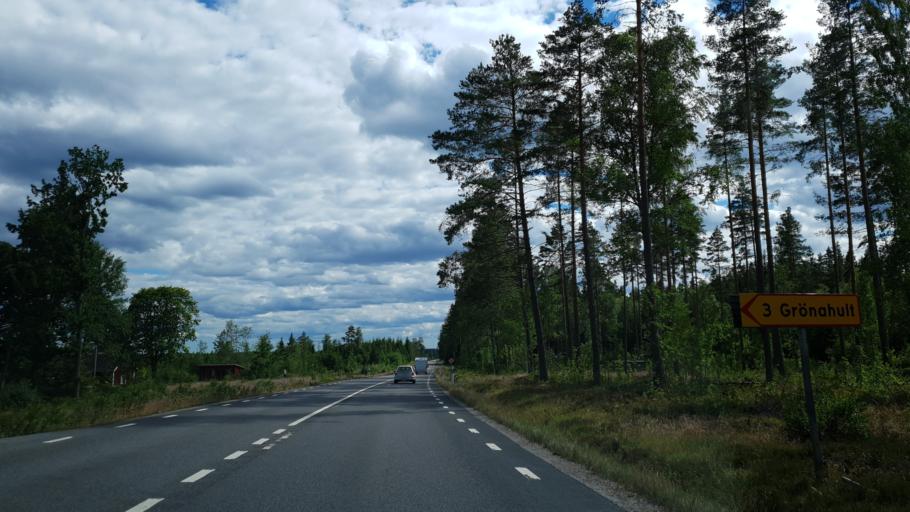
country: SE
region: Kronoberg
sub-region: Lessebo Kommun
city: Lessebo
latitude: 56.8164
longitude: 15.4111
